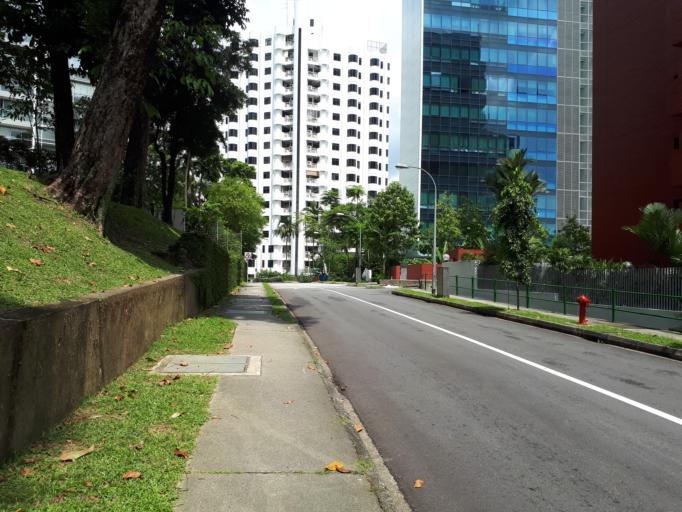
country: SG
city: Singapore
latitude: 1.3070
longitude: 103.8391
